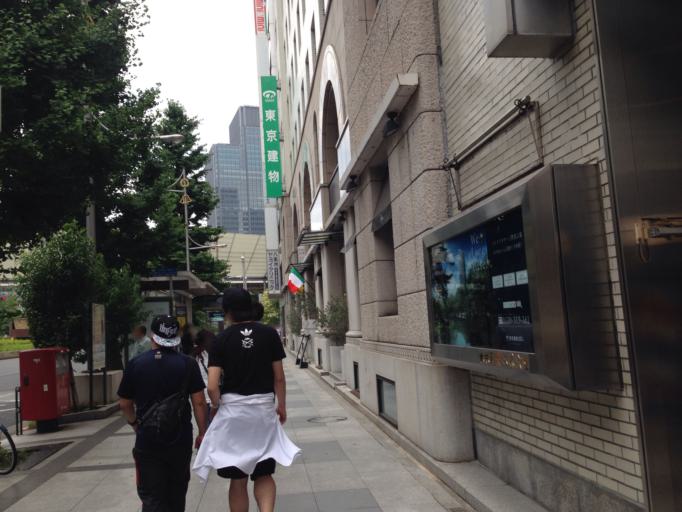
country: JP
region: Tokyo
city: Tokyo
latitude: 35.6799
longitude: 139.7704
